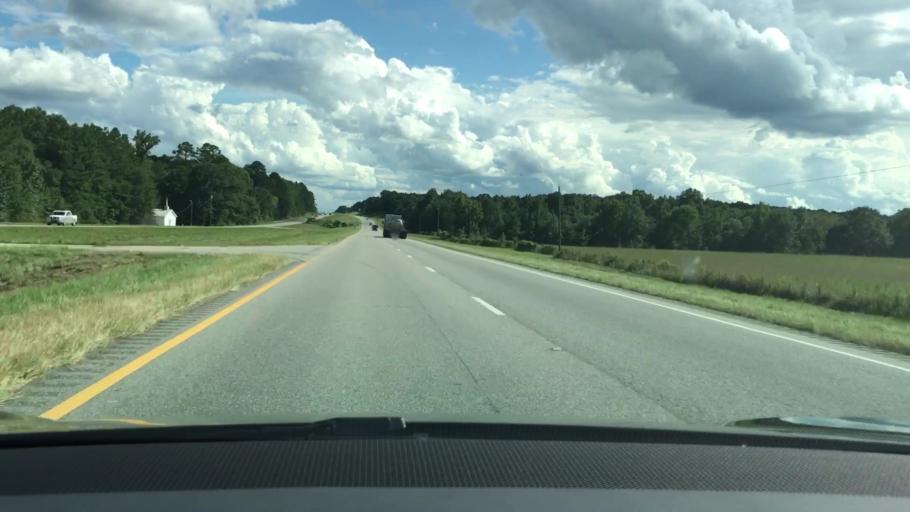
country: US
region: Alabama
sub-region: Montgomery County
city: Taylor
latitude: 32.0289
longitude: -86.0325
